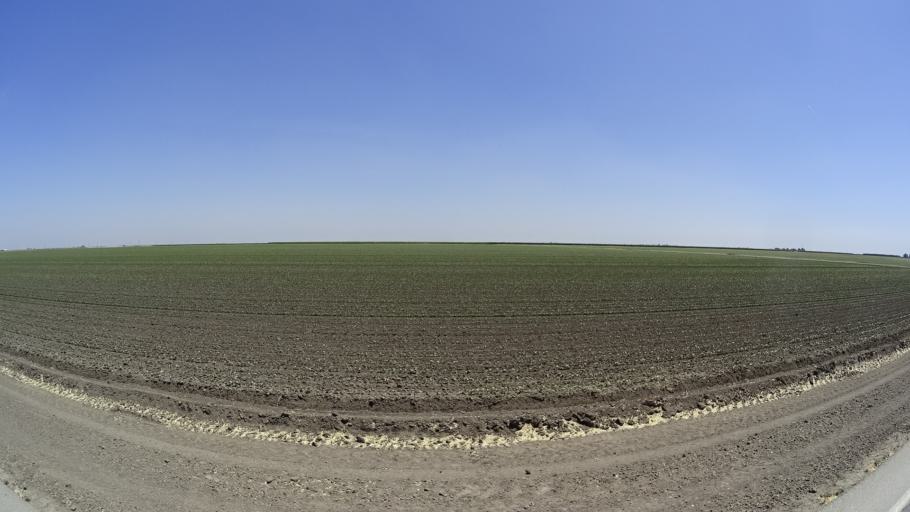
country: US
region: California
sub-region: Kings County
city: Corcoran
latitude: 36.1318
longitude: -119.6444
